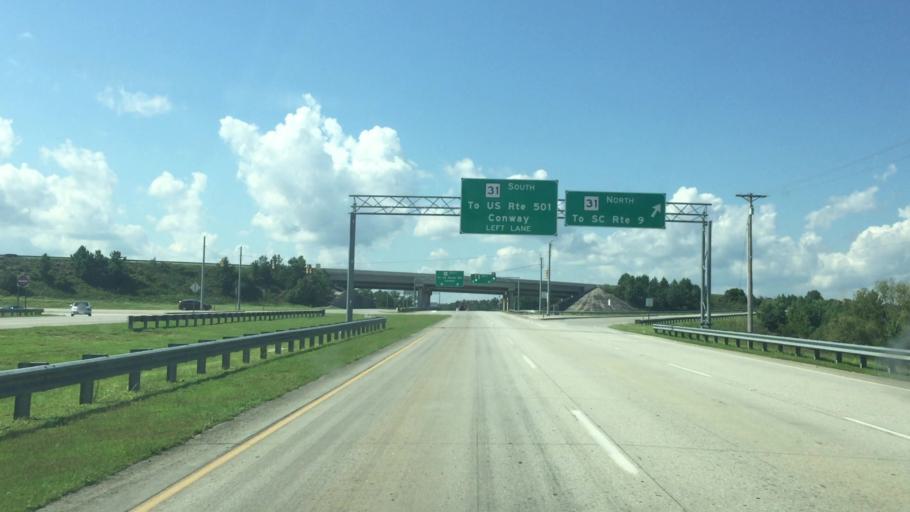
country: US
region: South Carolina
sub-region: Horry County
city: North Myrtle Beach
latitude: 33.8419
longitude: -78.7001
